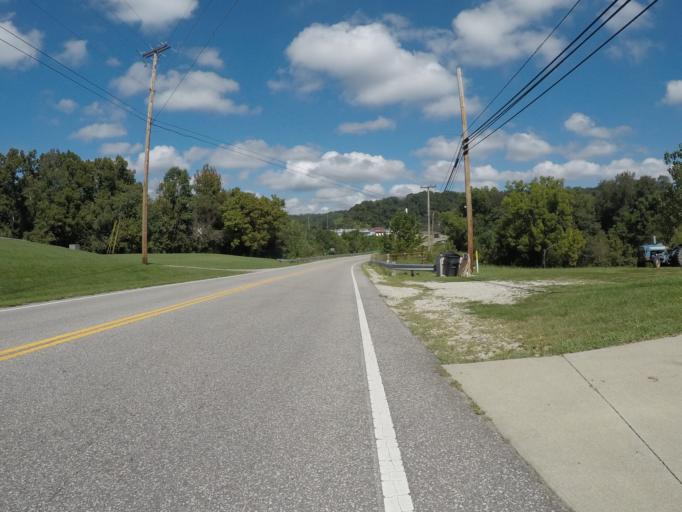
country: US
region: Ohio
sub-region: Lawrence County
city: Burlington
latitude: 38.4169
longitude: -82.5032
